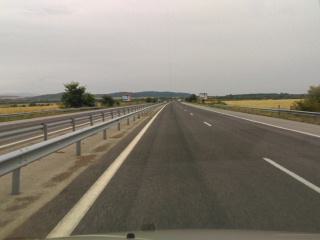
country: BG
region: Stara Zagora
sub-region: Obshtina Nikolaevo
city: Elkhovo
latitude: 42.3084
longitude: 25.5199
